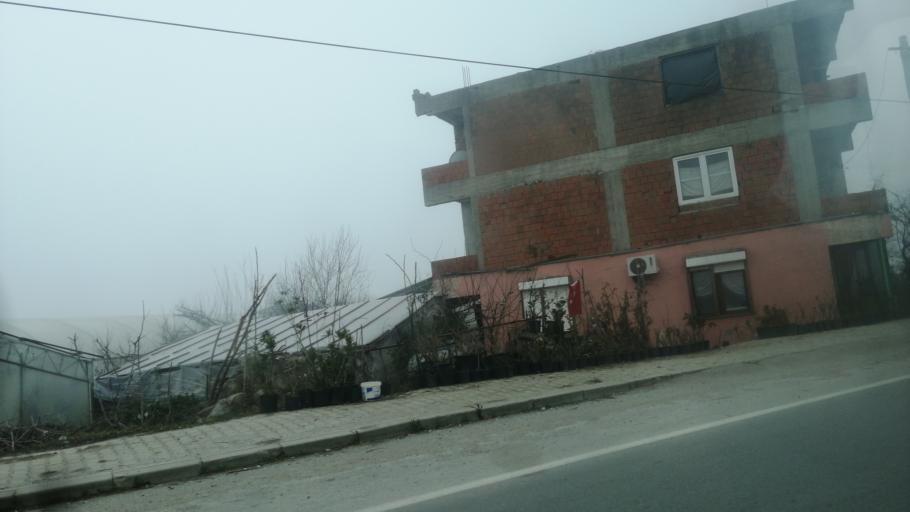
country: TR
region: Yalova
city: Korukoy
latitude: 40.6521
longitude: 29.1838
